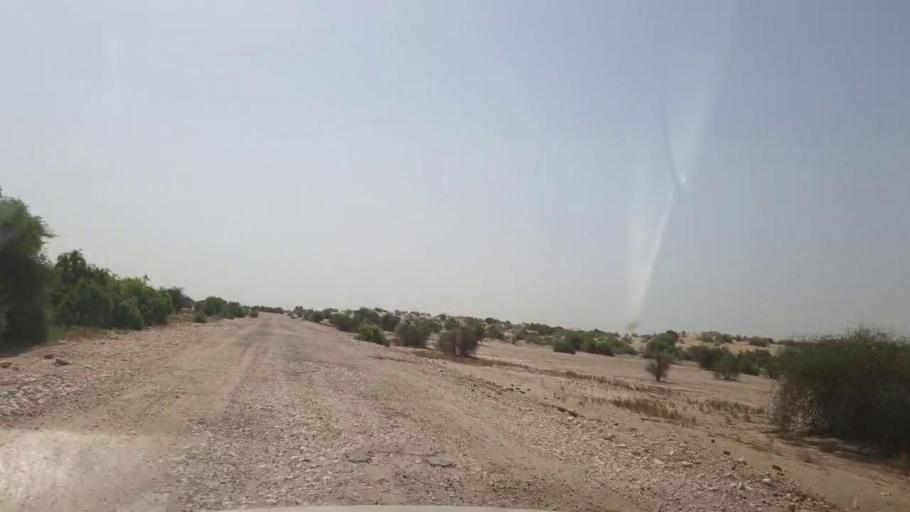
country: PK
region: Sindh
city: Rohri
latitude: 27.4368
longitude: 69.2455
